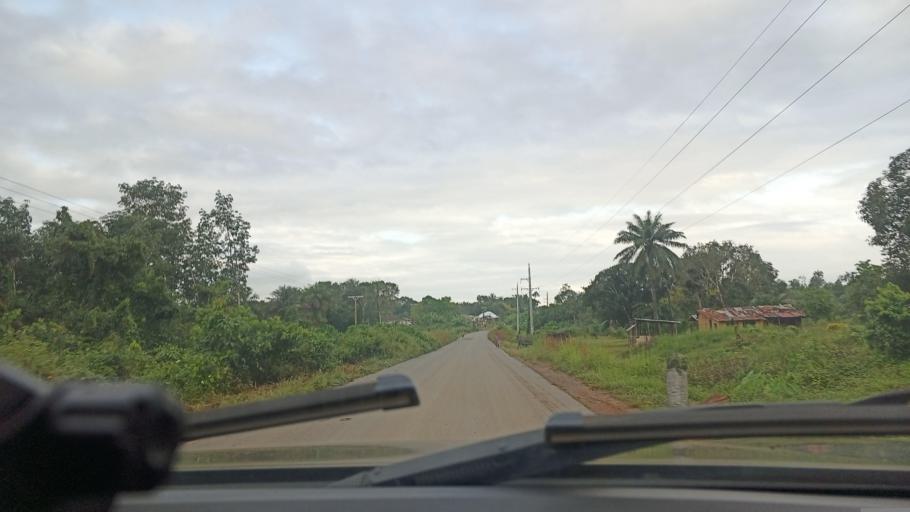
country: LR
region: Montserrado
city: Monrovia
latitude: 6.5613
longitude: -10.8710
